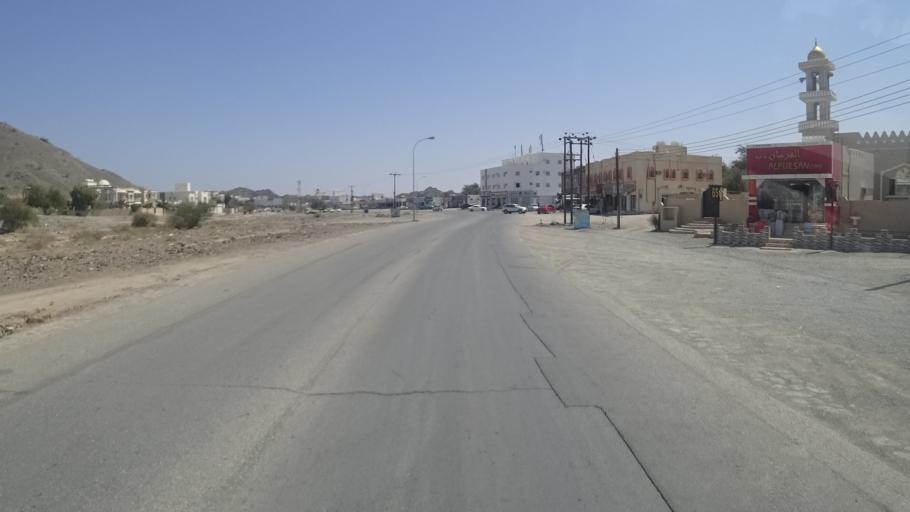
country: OM
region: Ash Sharqiyah
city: Ibra'
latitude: 22.6864
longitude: 58.5434
